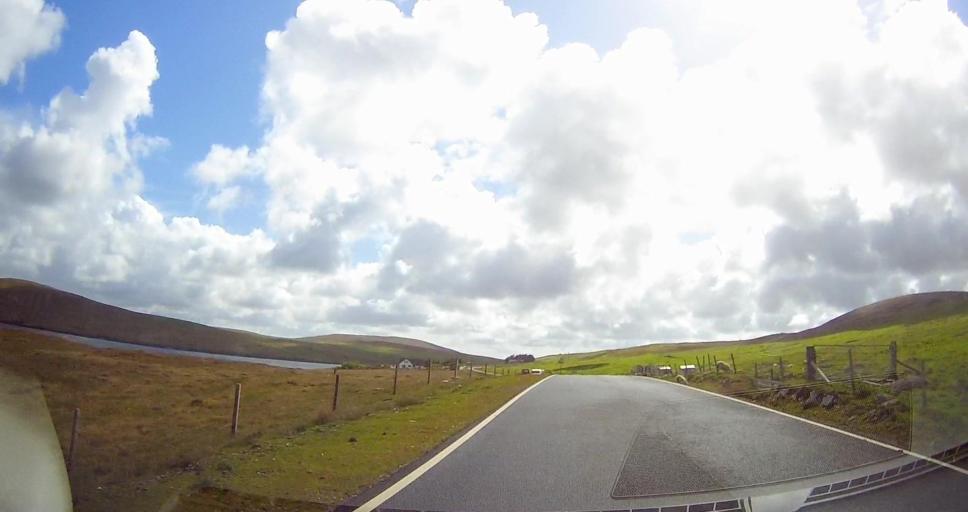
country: GB
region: Scotland
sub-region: Shetland Islands
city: Lerwick
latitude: 60.5394
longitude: -1.3539
